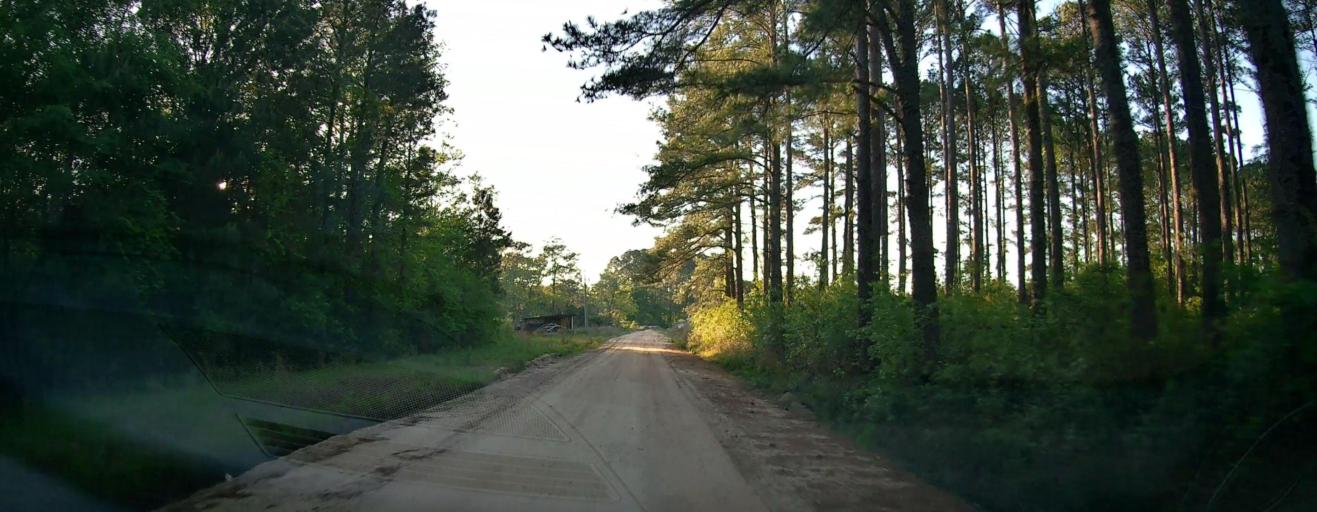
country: US
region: Georgia
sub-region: Irwin County
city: Ocilla
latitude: 31.6494
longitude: -83.2271
